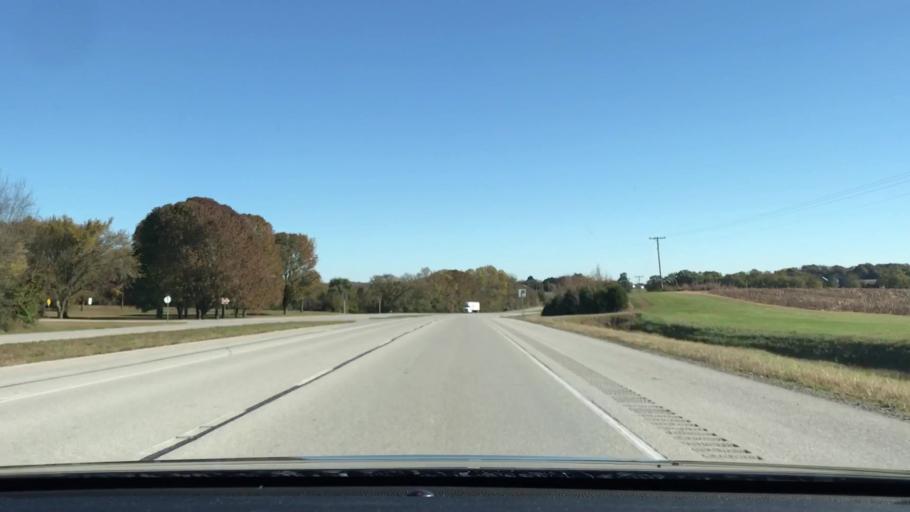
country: US
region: Kentucky
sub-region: Logan County
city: Auburn
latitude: 36.9065
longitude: -86.5859
